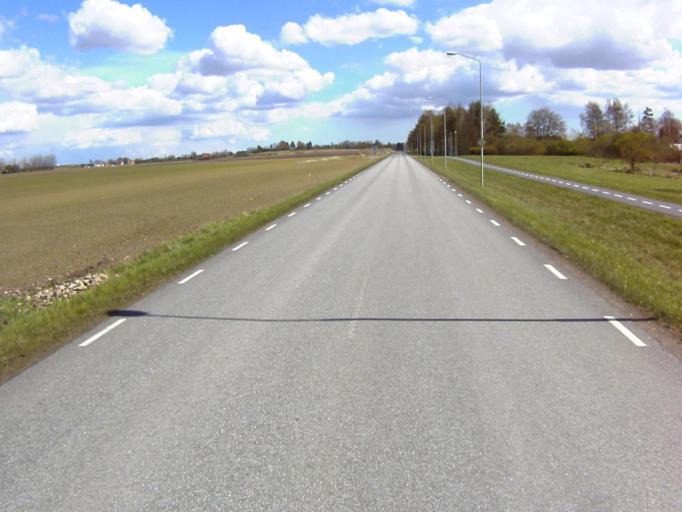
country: SE
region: Skane
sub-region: Kristianstads Kommun
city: Kristianstad
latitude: 56.0164
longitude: 14.0904
